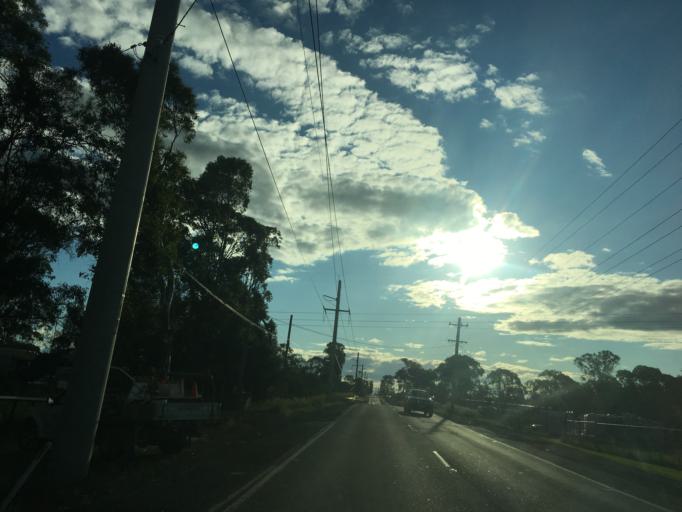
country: AU
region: New South Wales
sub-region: Fairfield
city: Cecil Park
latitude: -33.9163
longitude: 150.7968
